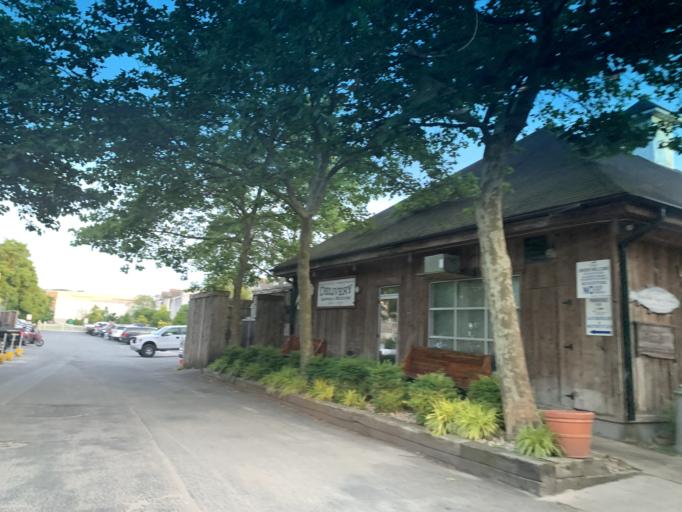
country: US
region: Maryland
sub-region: Harford County
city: Havre de Grace
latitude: 39.6045
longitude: -76.1161
